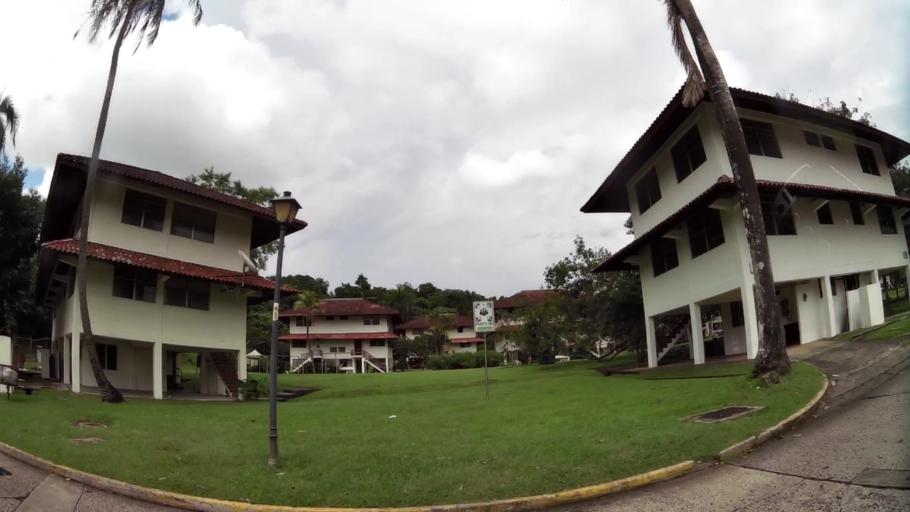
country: PA
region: Panama
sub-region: Distrito de Panama
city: Paraiso
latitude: 9.0033
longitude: -79.5834
